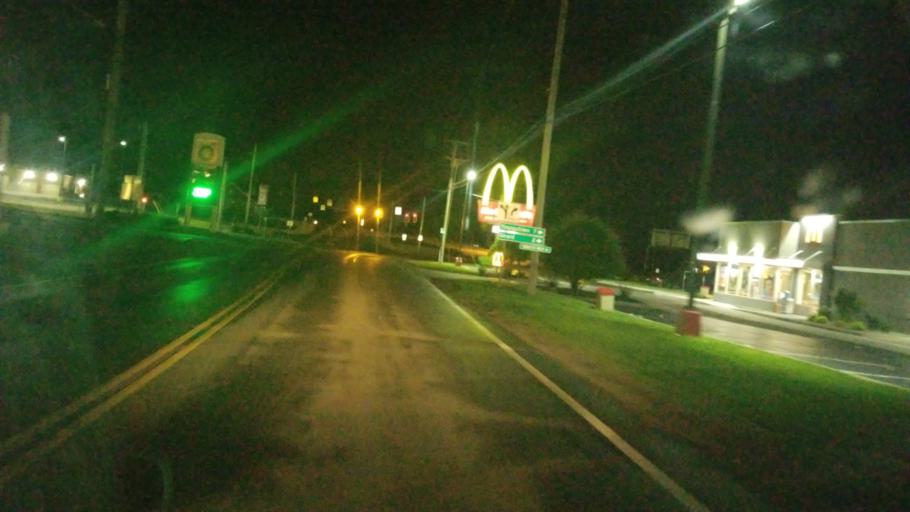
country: US
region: Ohio
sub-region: Trumbull County
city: McKinley Heights
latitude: 41.1820
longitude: -80.7188
